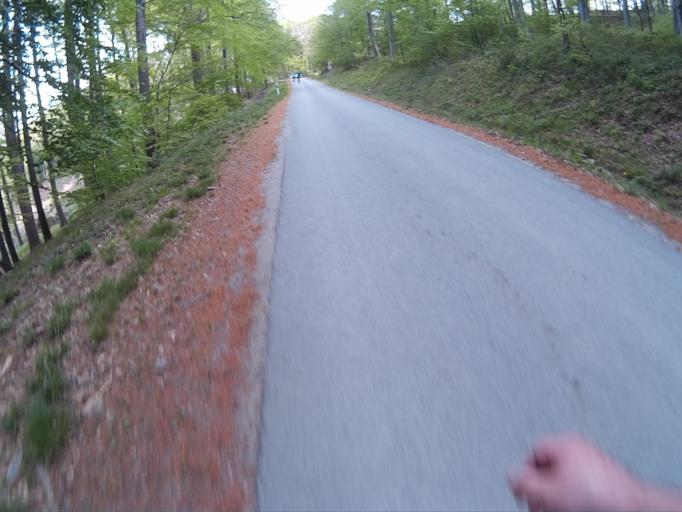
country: AT
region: Burgenland
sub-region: Politischer Bezirk Oberwart
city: Rechnitz
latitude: 47.3537
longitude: 16.4729
